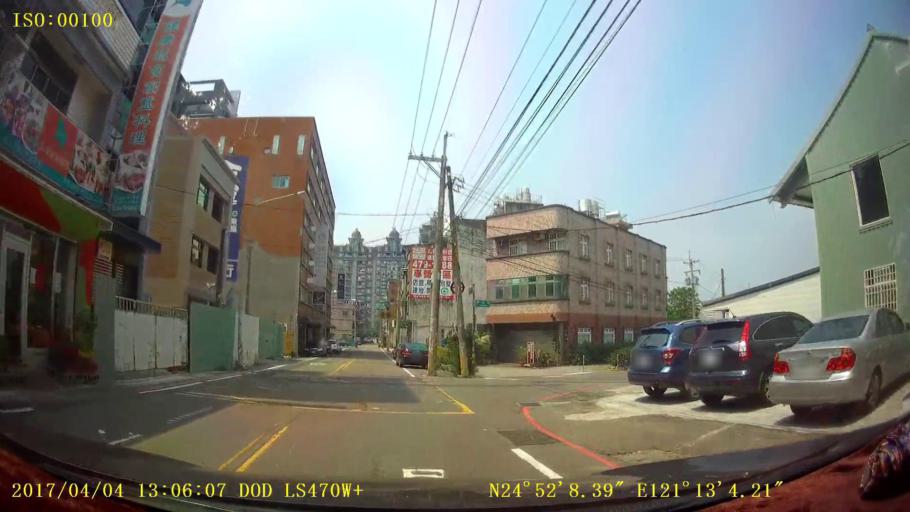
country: TW
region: Taiwan
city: Daxi
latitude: 24.8692
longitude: 121.2178
